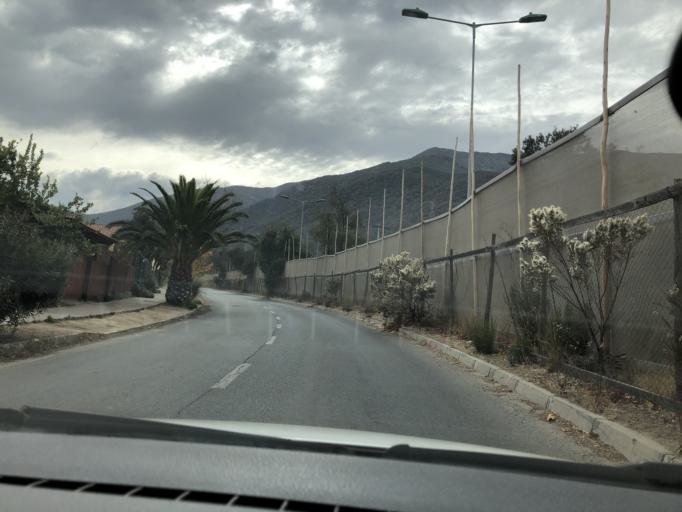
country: CL
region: Santiago Metropolitan
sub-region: Provincia de Cordillera
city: Puente Alto
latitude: -33.5853
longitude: -70.5062
